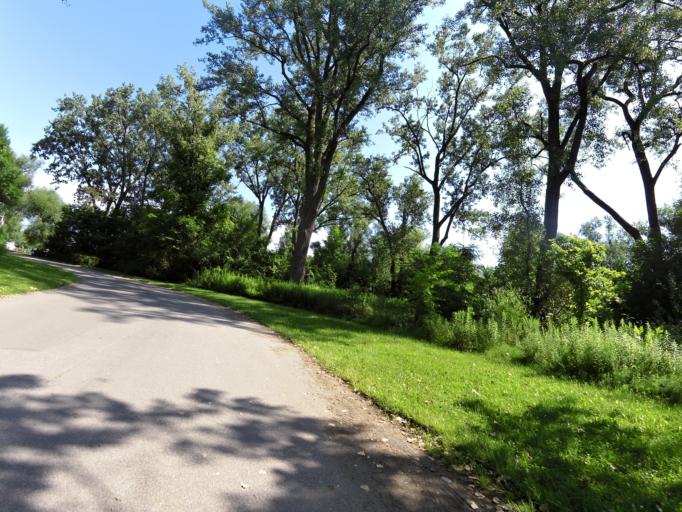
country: CA
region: Ontario
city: Toronto
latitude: 43.6156
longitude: -79.3893
